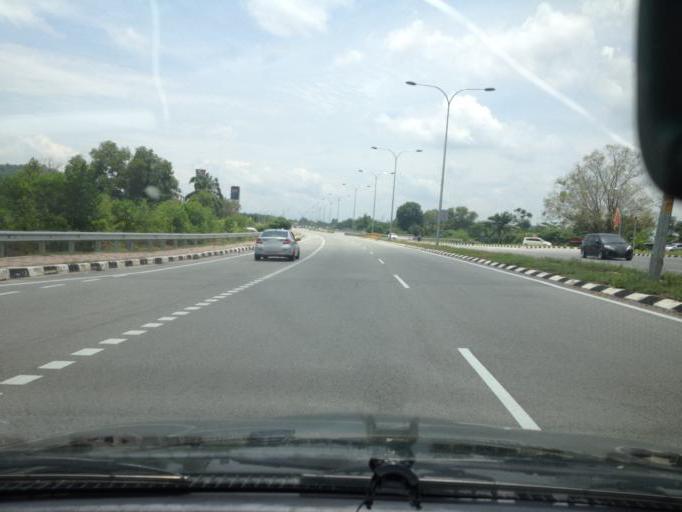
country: MY
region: Kedah
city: Sungai Petani
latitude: 5.6225
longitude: 100.5368
